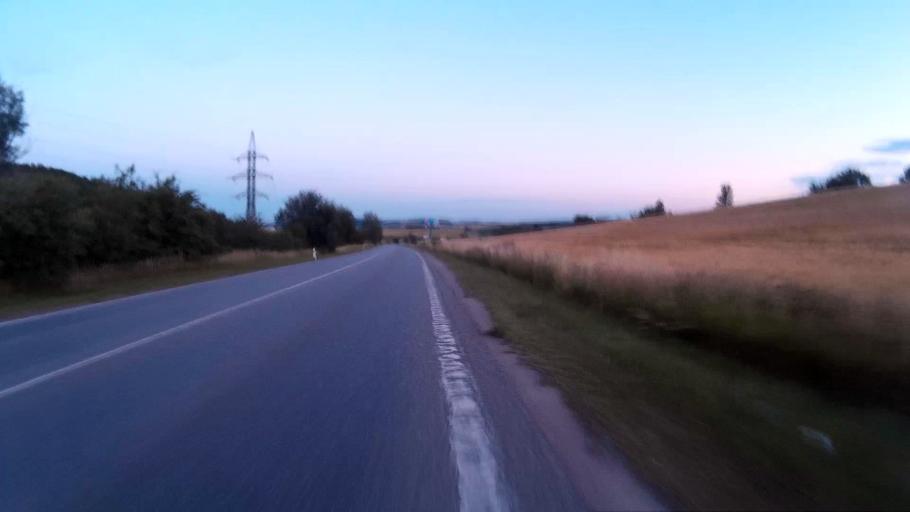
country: CZ
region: South Moravian
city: Troubsko
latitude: 49.1895
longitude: 16.5073
